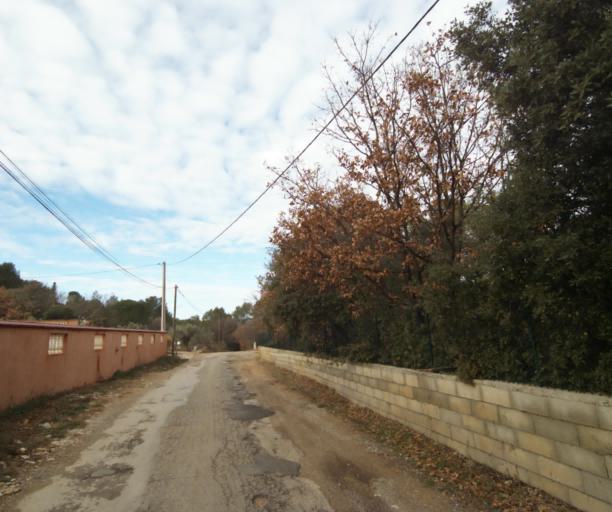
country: FR
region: Provence-Alpes-Cote d'Azur
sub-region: Departement du Var
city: Trans-en-Provence
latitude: 43.5148
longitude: 6.4942
